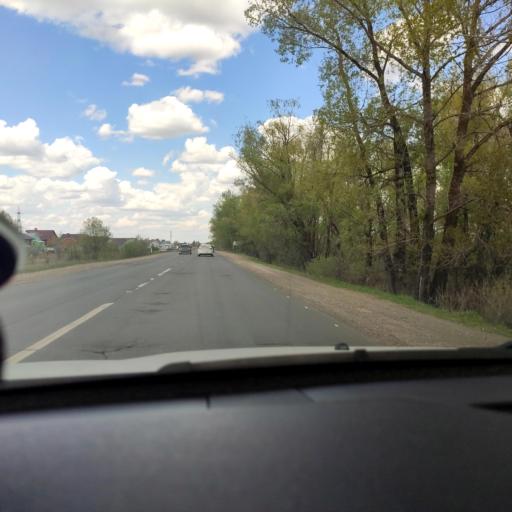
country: RU
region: Samara
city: Kinel'
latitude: 53.2005
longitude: 50.6371
